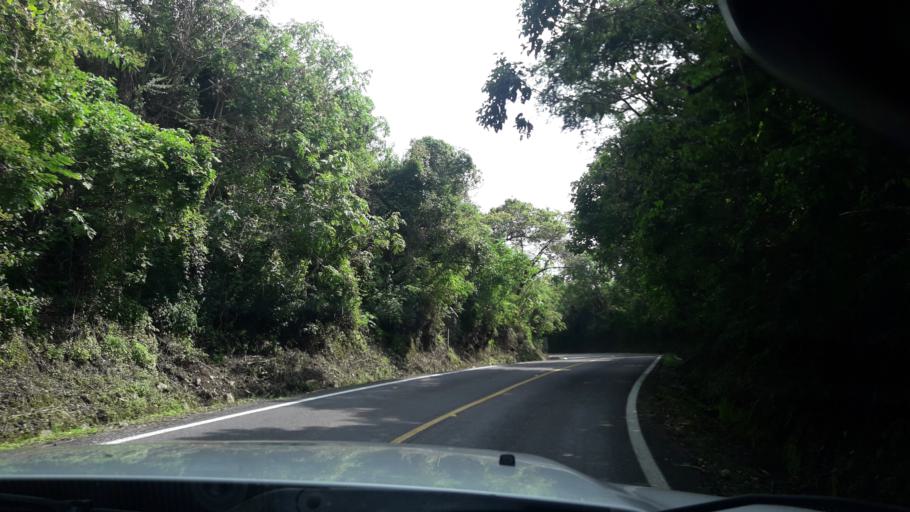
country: MX
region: Colima
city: Suchitlan
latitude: 19.4356
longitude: -103.7039
